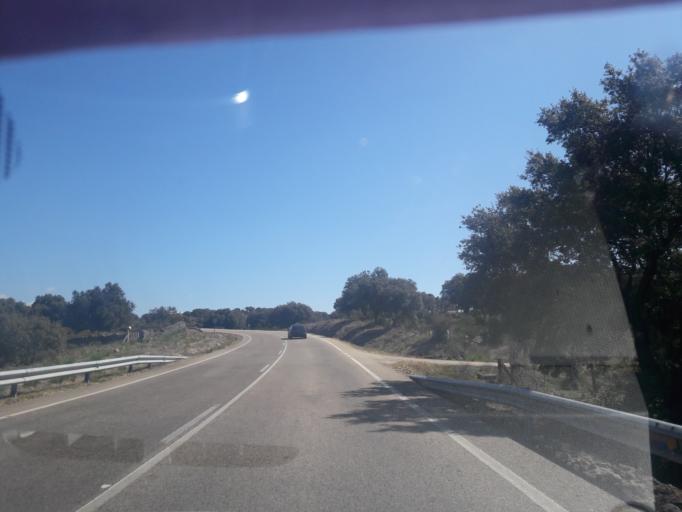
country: ES
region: Castille and Leon
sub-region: Provincia de Salamanca
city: Encina de San Silvestre
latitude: 41.0382
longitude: -6.0859
